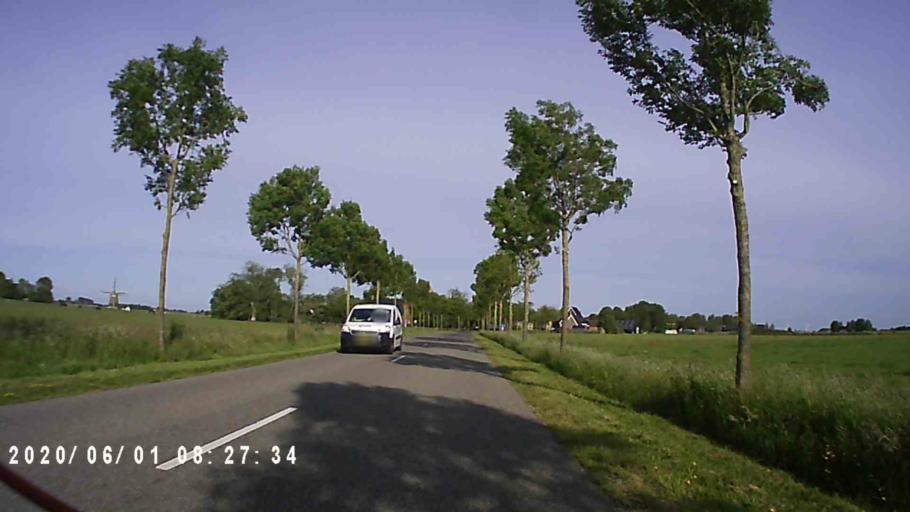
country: NL
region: Friesland
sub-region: Gemeente Ferwerderadiel
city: Burdaard
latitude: 53.3004
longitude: 5.8552
